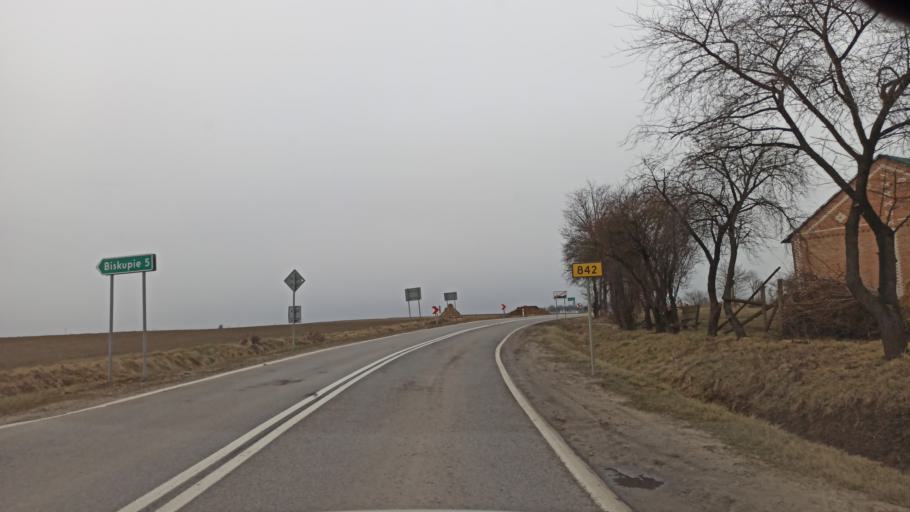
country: PL
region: Lublin Voivodeship
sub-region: Powiat lubelski
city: Wysokie
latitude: 50.9058
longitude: 22.6641
